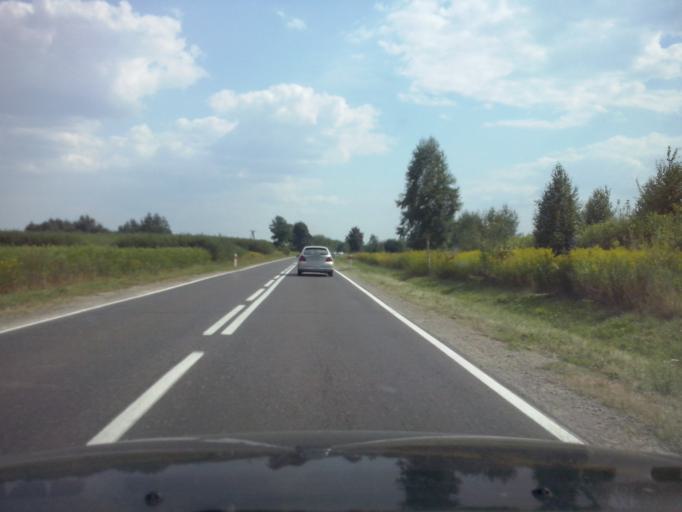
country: PL
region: Subcarpathian Voivodeship
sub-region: Powiat nizanski
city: Rudnik nad Sanem
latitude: 50.4692
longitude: 22.2395
